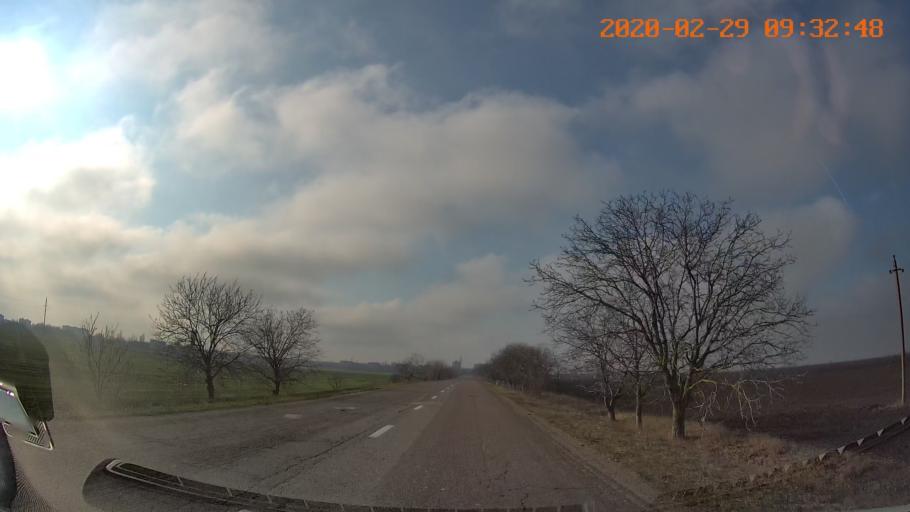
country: MD
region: Telenesti
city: Dnestrovsc
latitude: 46.6348
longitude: 29.9042
